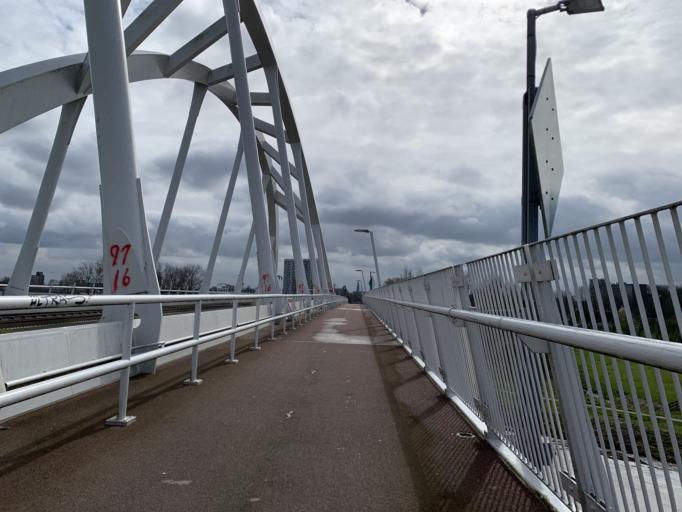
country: NL
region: Groningen
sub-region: Gemeente Groningen
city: Korrewegwijk
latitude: 53.2429
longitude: 6.5566
